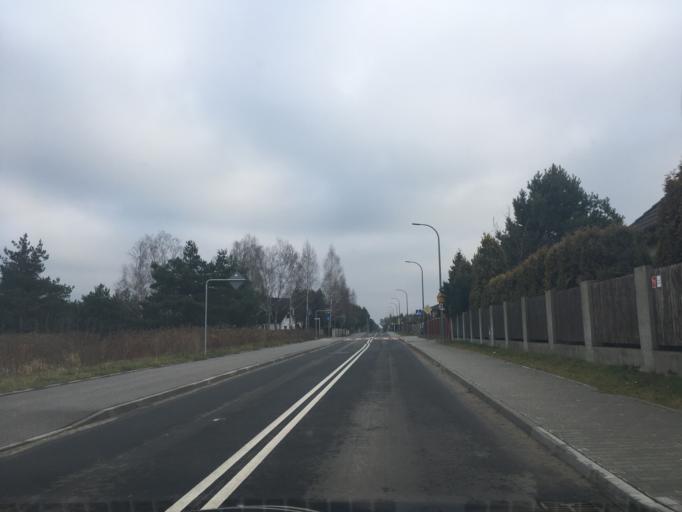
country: PL
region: Masovian Voivodeship
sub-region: Powiat piaseczynski
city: Lesznowola
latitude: 52.0715
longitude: 20.9688
